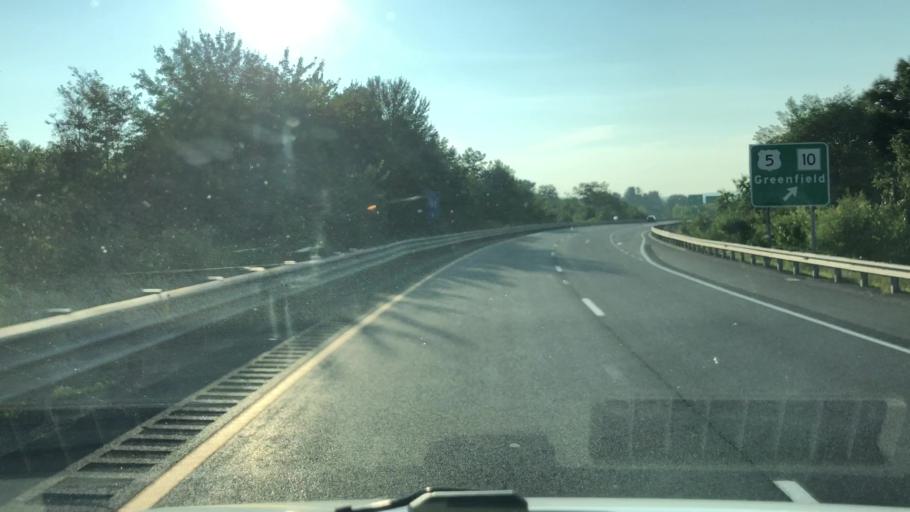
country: US
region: Massachusetts
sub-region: Franklin County
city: Turners Falls
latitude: 42.6087
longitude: -72.5809
